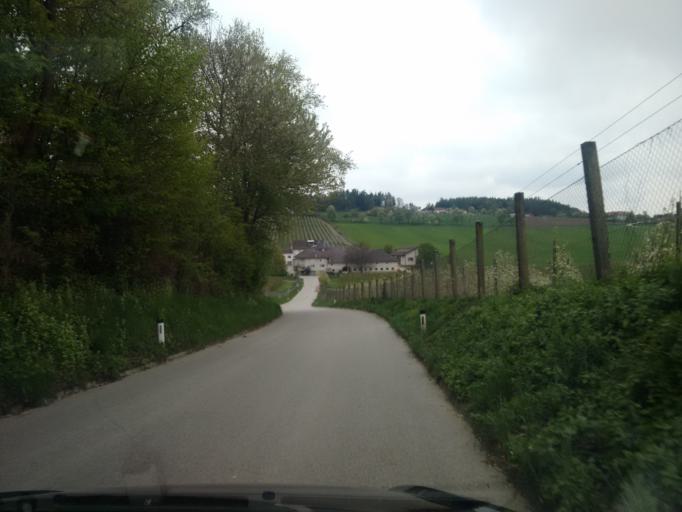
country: AT
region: Upper Austria
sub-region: Wels-Land
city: Buchkirchen
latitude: 48.2380
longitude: 14.0567
